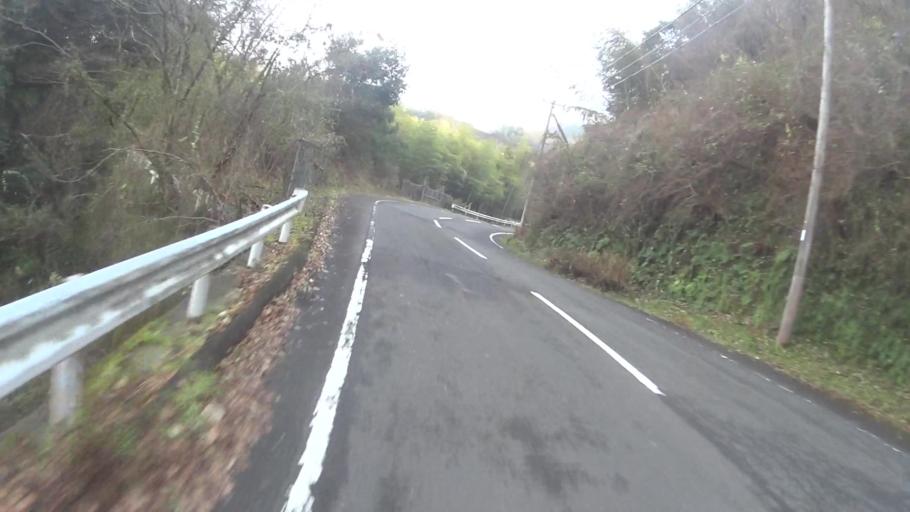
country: JP
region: Kyoto
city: Maizuru
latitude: 35.4430
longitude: 135.3941
